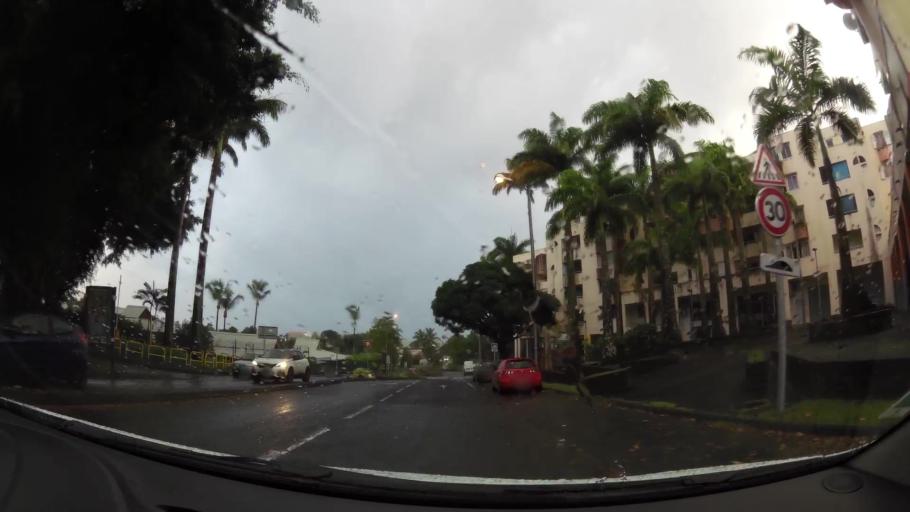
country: RE
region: Reunion
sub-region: Reunion
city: Saint-Benoit
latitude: -21.0392
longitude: 55.7105
